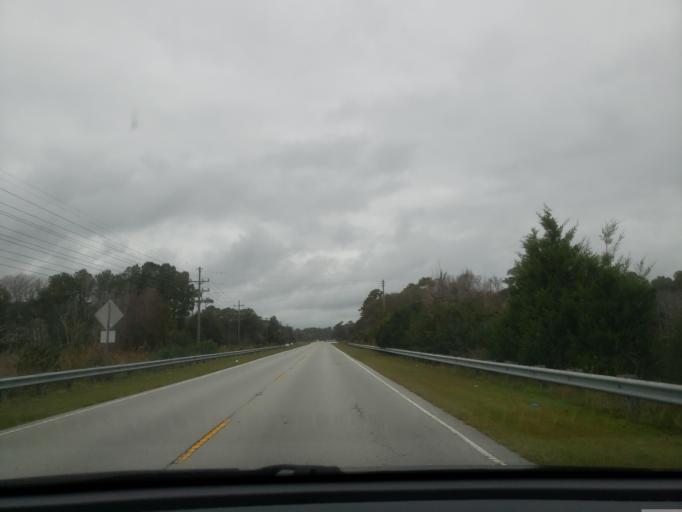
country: US
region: North Carolina
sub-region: Onslow County
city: Sneads Ferry
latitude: 34.5063
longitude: -77.4323
